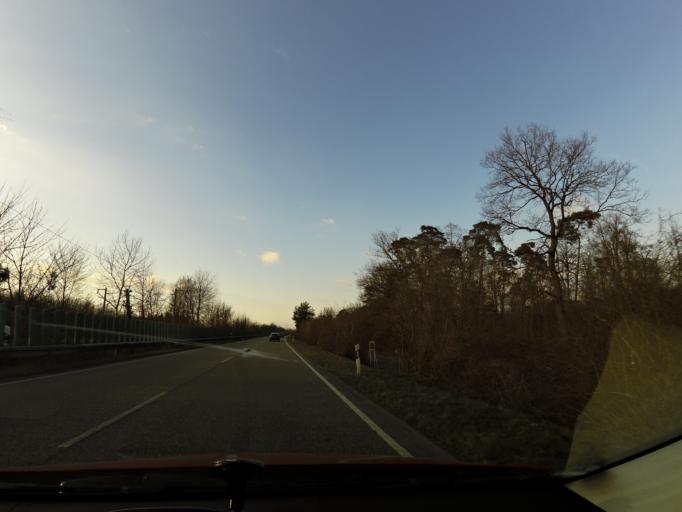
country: DE
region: Baden-Wuerttemberg
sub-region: Karlsruhe Region
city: Hambrucken
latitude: 49.2069
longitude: 8.5032
